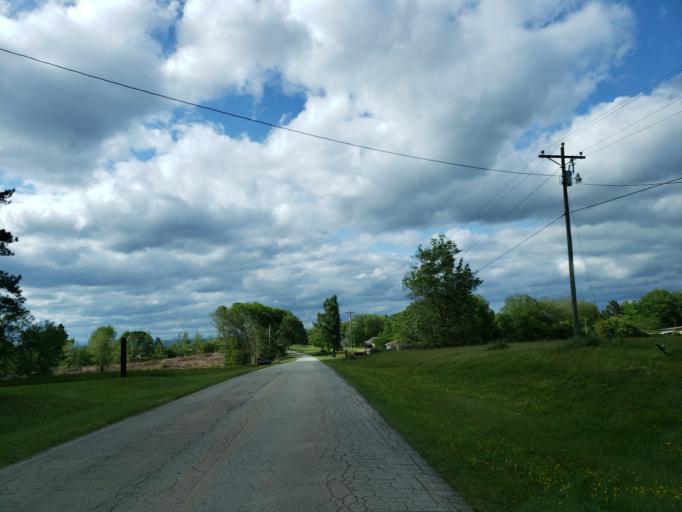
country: US
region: Georgia
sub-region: Haralson County
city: Tallapoosa
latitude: 33.6705
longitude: -85.2894
